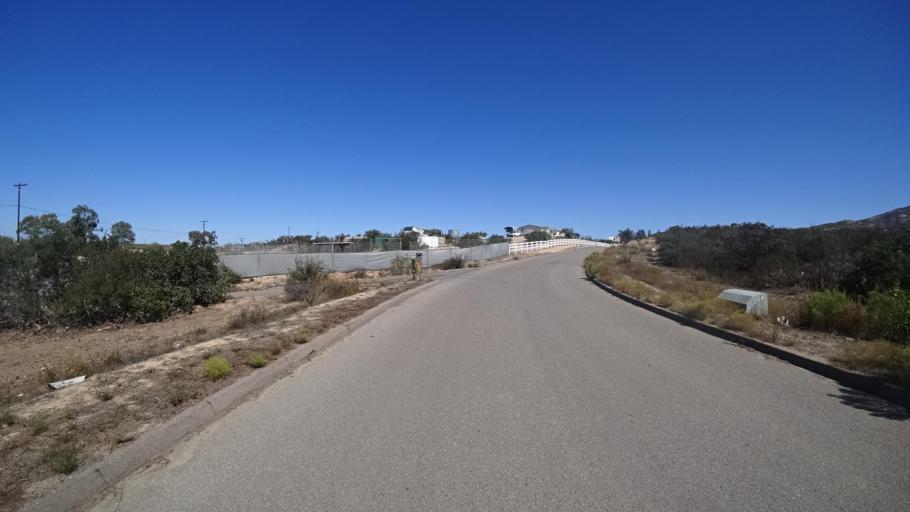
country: US
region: California
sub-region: San Diego County
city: Alpine
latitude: 32.7640
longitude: -116.7706
